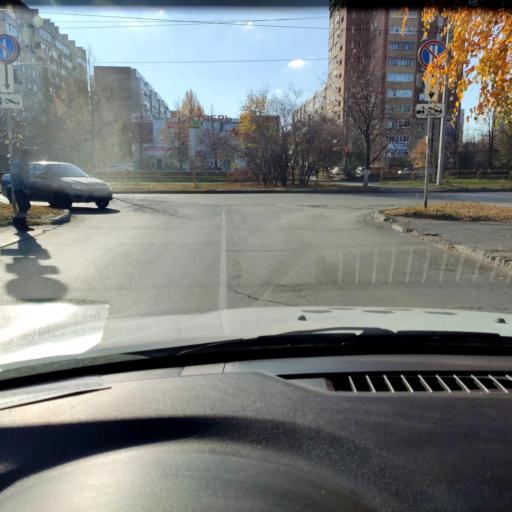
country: RU
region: Samara
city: Tol'yatti
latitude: 53.5411
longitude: 49.3522
